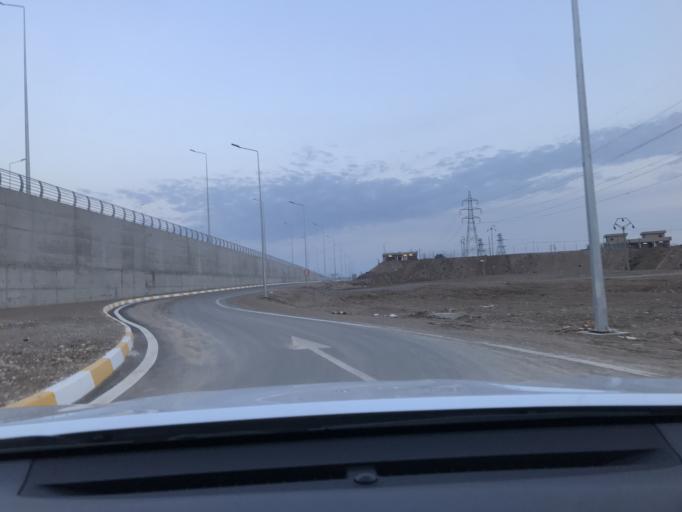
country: IQ
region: Arbil
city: Erbil
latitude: 36.3146
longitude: 43.9110
